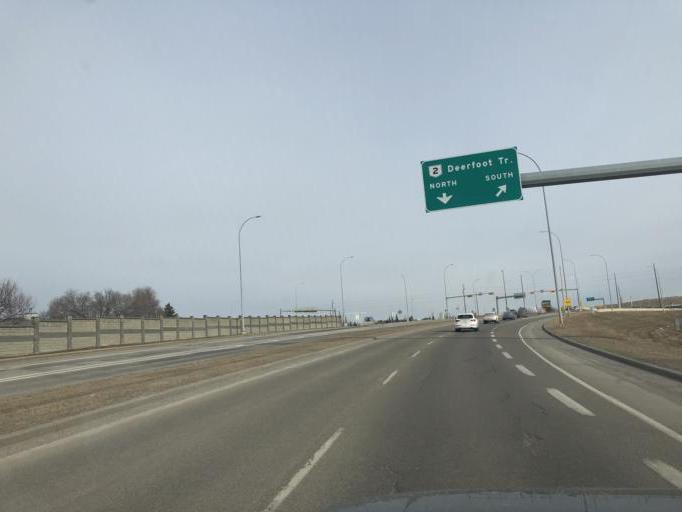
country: CA
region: Alberta
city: Calgary
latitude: 50.9460
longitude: -114.0052
